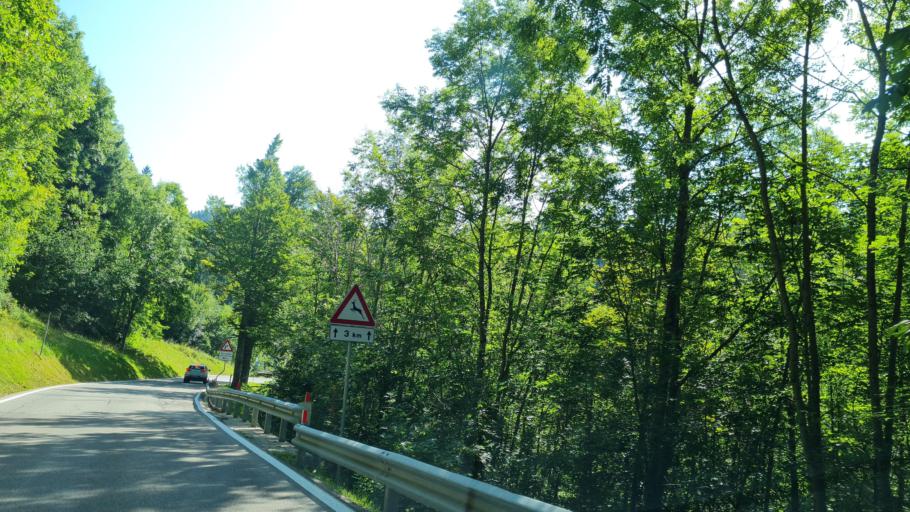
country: IT
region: Trentino-Alto Adige
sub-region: Provincia di Trento
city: Folgaria
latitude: 45.9111
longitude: 11.1795
